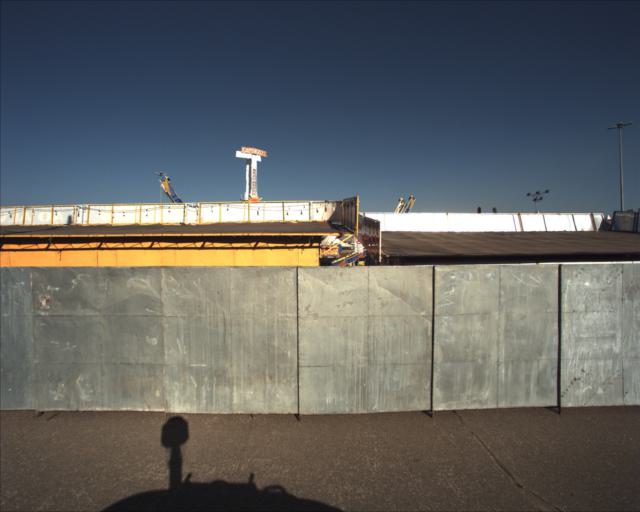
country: BR
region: Sao Paulo
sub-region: Sorocaba
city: Sorocaba
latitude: -23.4685
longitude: -47.4455
